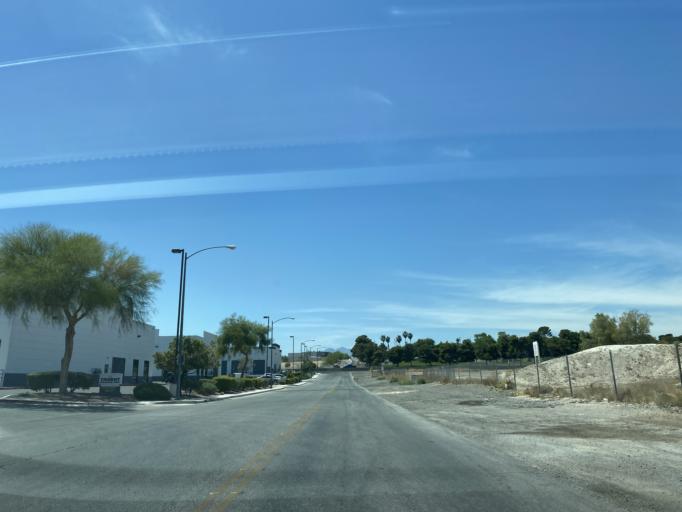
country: US
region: Nevada
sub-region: Clark County
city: North Las Vegas
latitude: 36.2140
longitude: -115.1314
